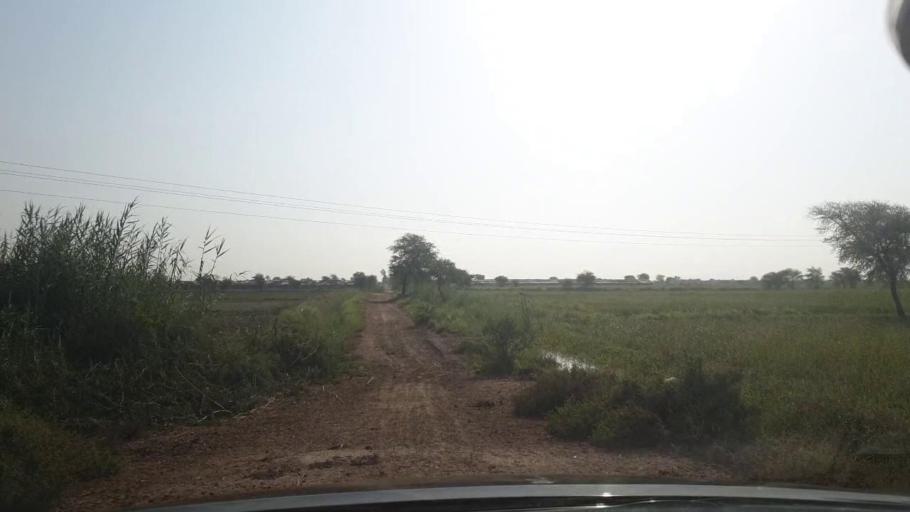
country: PK
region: Sindh
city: Kadhan
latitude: 24.6451
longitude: 69.1485
